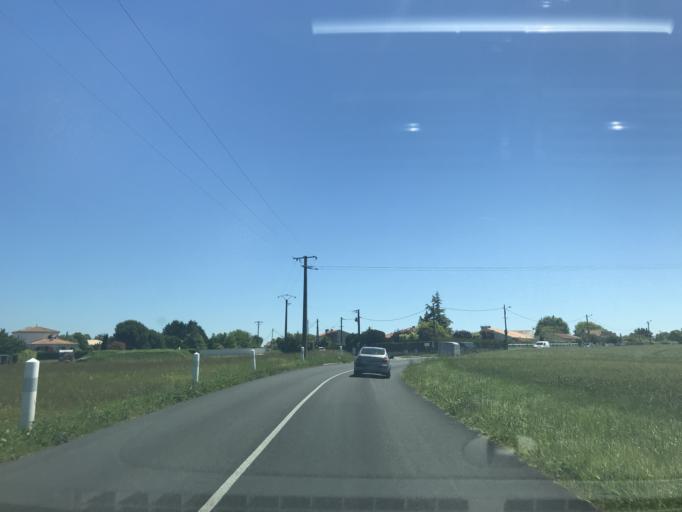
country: FR
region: Poitou-Charentes
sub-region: Departement de la Charente-Maritime
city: Meschers-sur-Gironde
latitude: 45.5864
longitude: -0.9601
